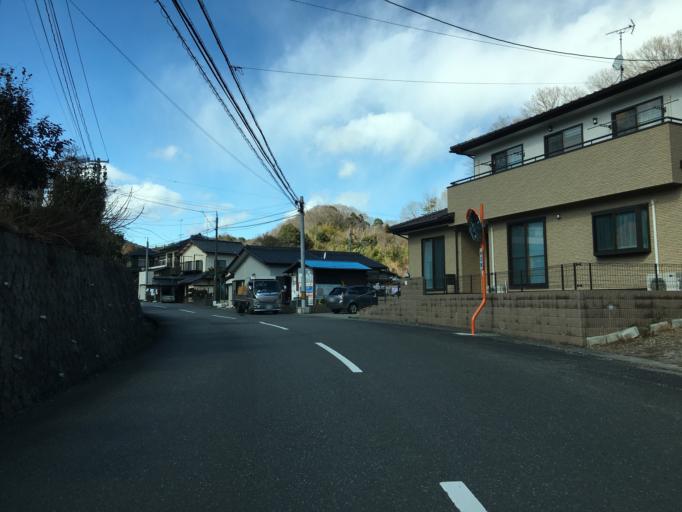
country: JP
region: Fukushima
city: Iwaki
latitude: 37.0119
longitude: 140.8249
